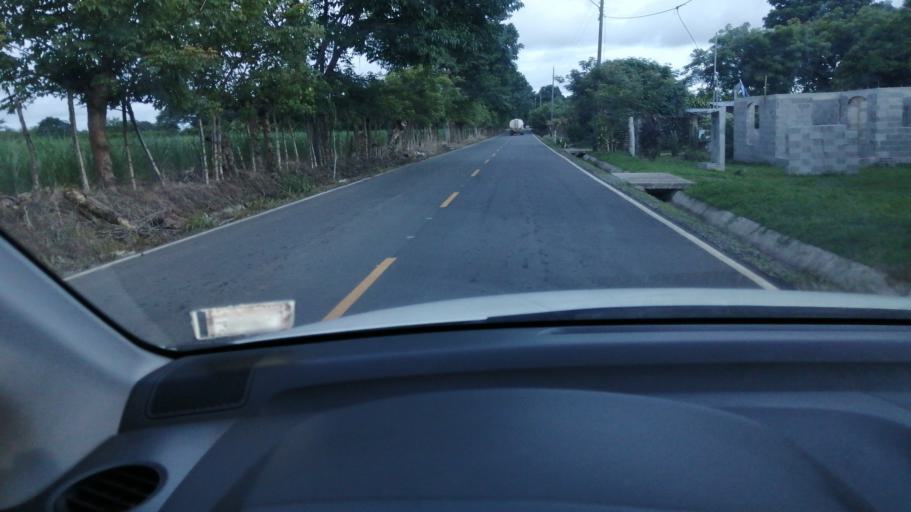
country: PA
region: Chiriqui
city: Alanje
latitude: 8.4146
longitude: -82.5186
